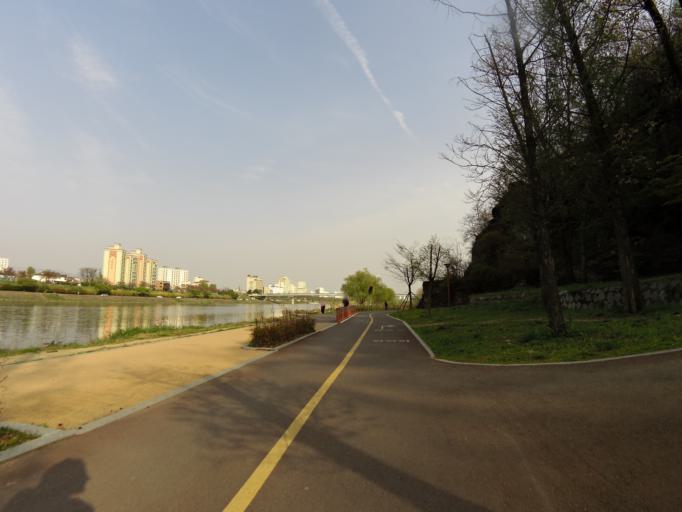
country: KR
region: Daegu
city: Daegu
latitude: 35.8866
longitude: 128.6444
